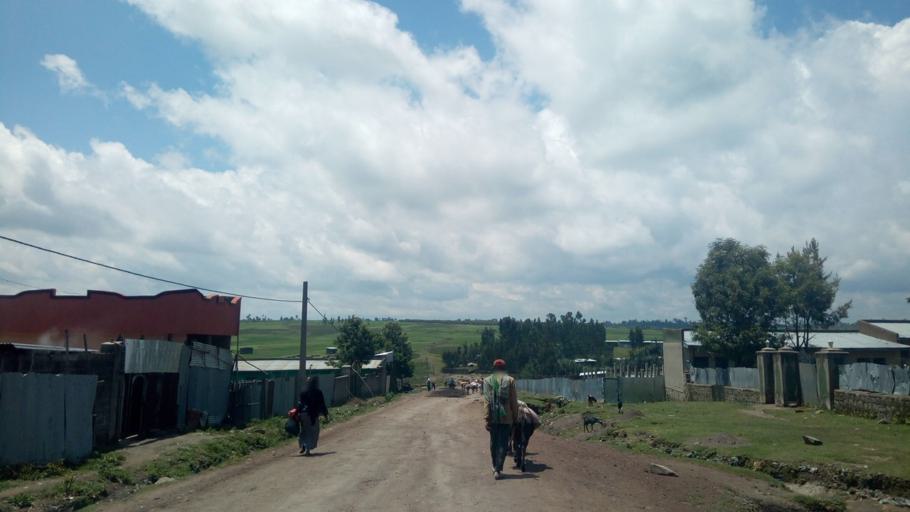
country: ET
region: Oromiya
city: Sendafa
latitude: 8.9724
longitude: 39.1195
